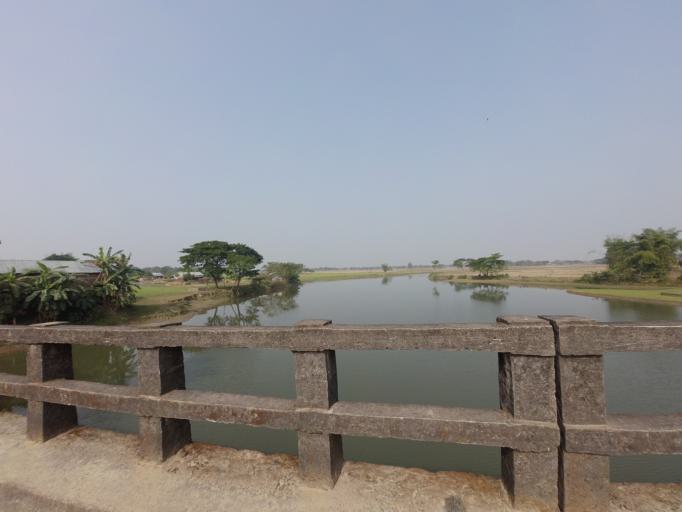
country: BD
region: Dhaka
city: Netrakona
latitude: 25.0093
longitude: 90.6835
